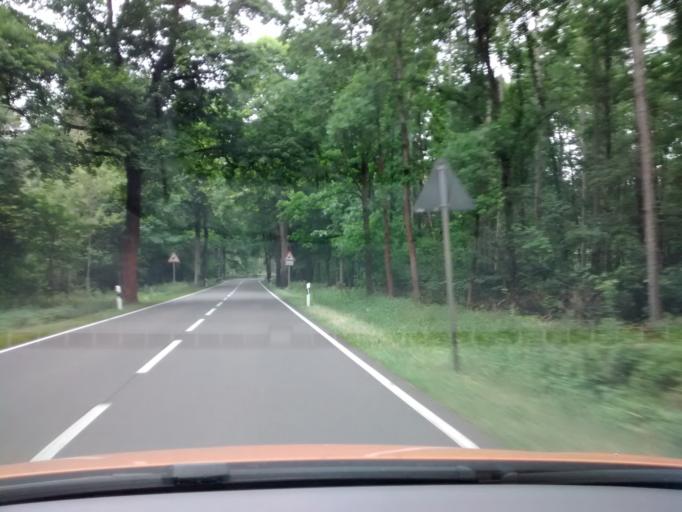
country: DE
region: Brandenburg
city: Wiesenburg
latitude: 52.0912
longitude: 12.4405
